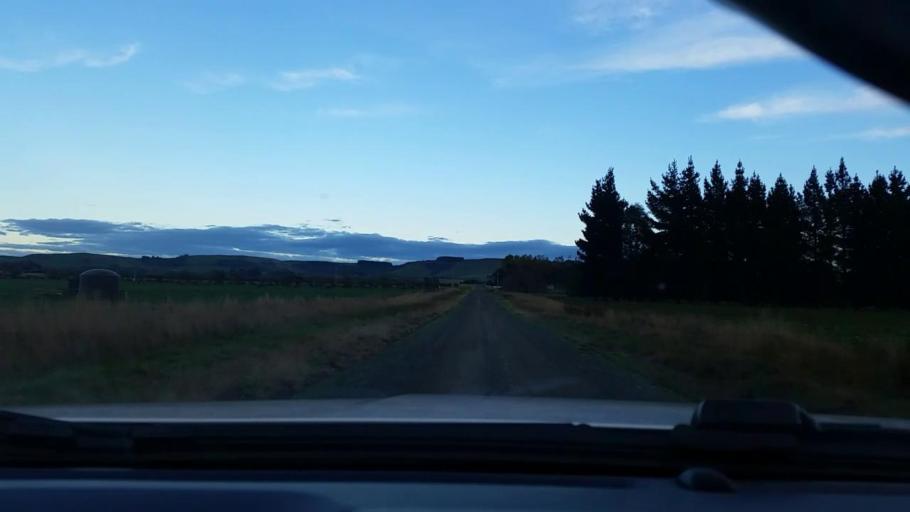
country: NZ
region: Southland
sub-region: Southland District
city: Winton
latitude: -46.1063
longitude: 168.4506
